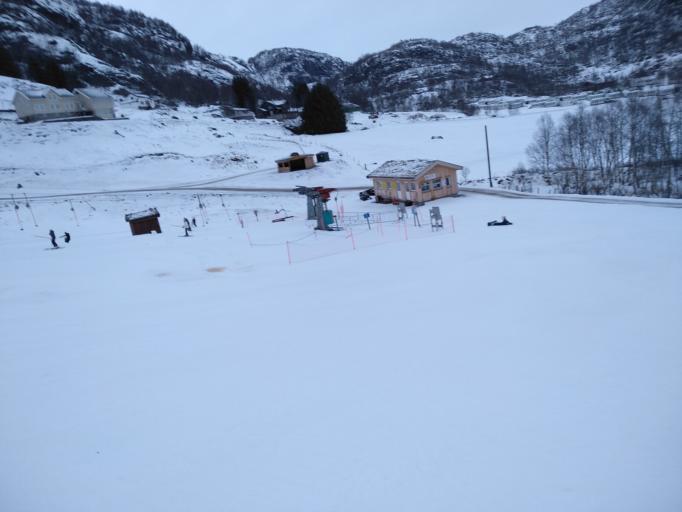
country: NO
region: Vest-Agder
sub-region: Sirdal
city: Tonstad
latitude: 59.0217
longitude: 6.9220
